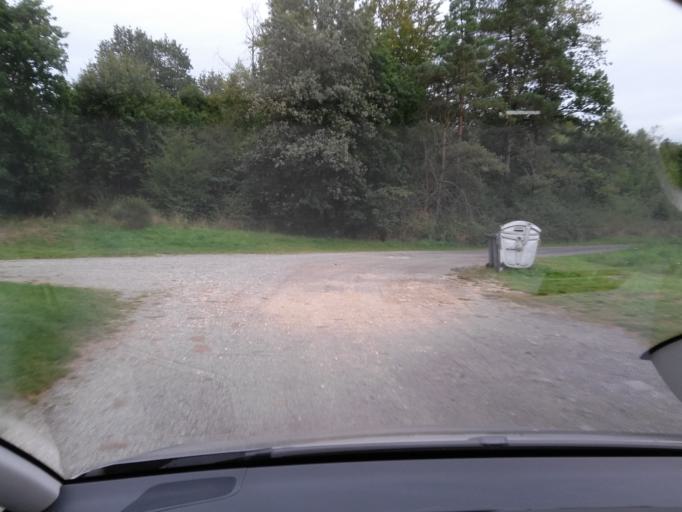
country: BE
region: Wallonia
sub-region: Province du Luxembourg
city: Etalle
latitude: 49.6644
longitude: 5.5757
